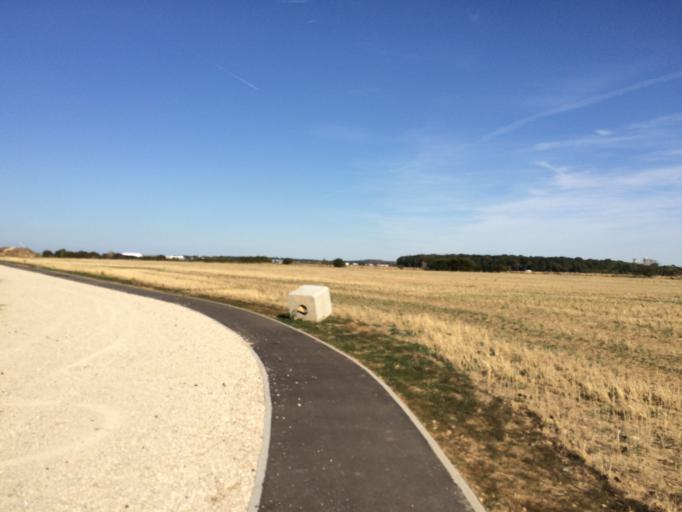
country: FR
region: Ile-de-France
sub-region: Departement de l'Essonne
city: Le Plessis-Pate
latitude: 48.5918
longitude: 2.3166
